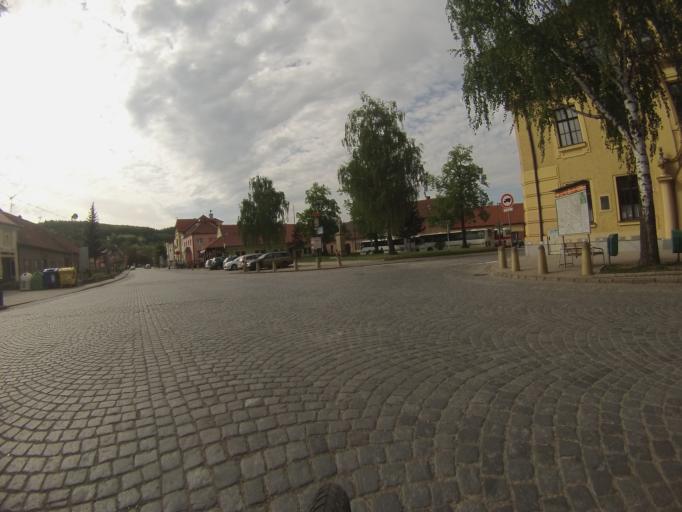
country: CZ
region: South Moravian
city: Veverska Bityska
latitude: 49.2758
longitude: 16.4368
